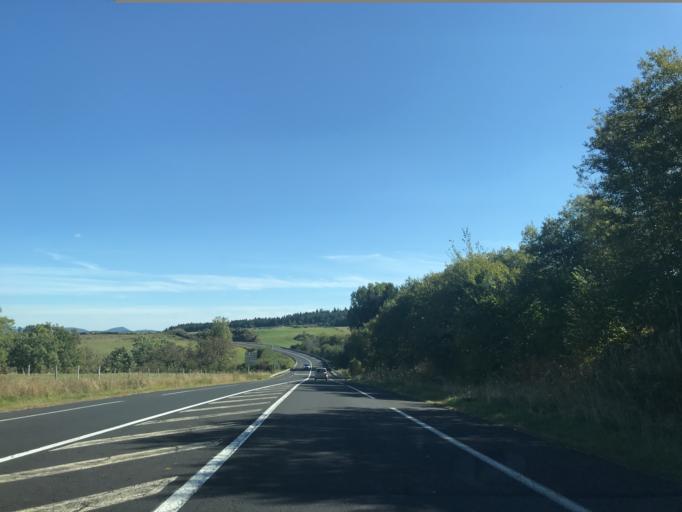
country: FR
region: Auvergne
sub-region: Departement du Puy-de-Dome
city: La Bourboule
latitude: 45.6603
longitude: 2.7648
